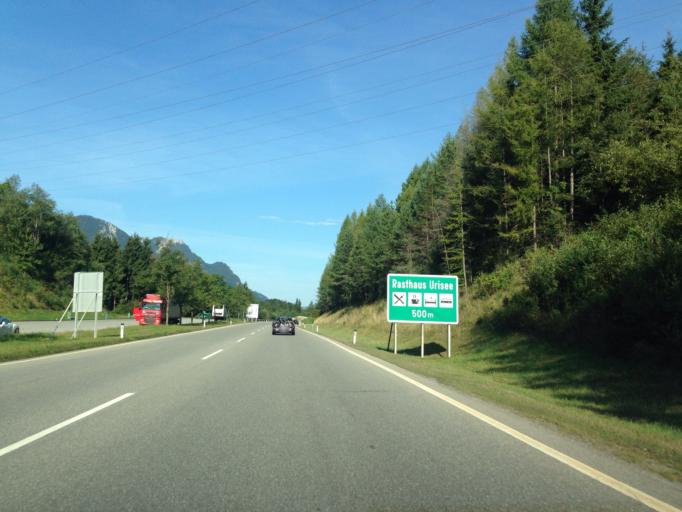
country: AT
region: Tyrol
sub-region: Politischer Bezirk Reutte
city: Breitenwang
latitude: 47.4973
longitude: 10.7421
